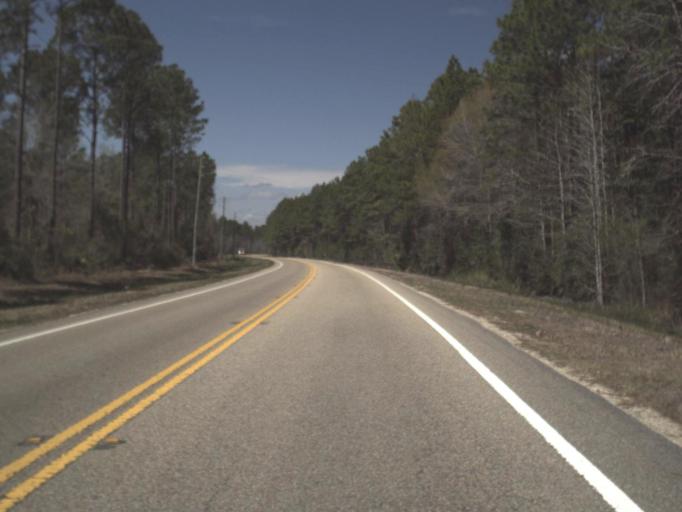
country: US
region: Florida
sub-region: Leon County
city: Woodville
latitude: 30.2085
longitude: -84.1910
